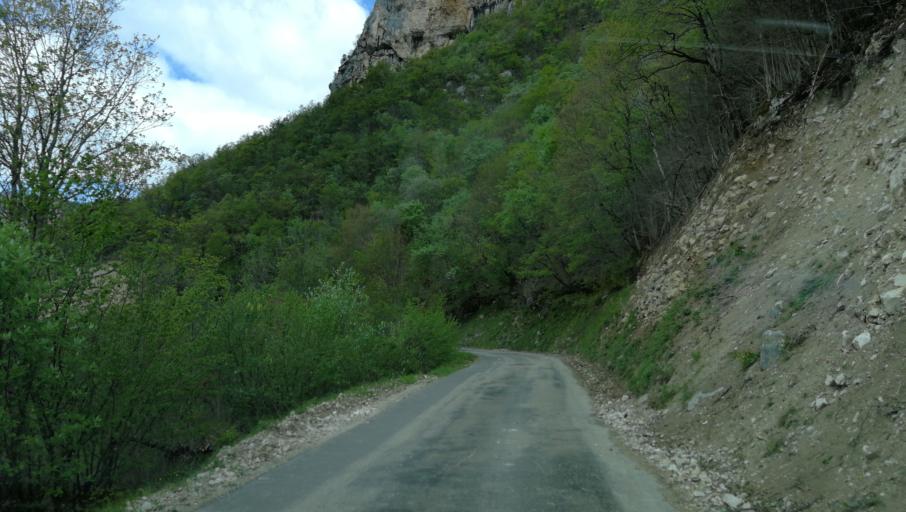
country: FR
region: Rhone-Alpes
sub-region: Departement de l'Isere
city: Pont-en-Royans
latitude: 45.0647
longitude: 5.4089
